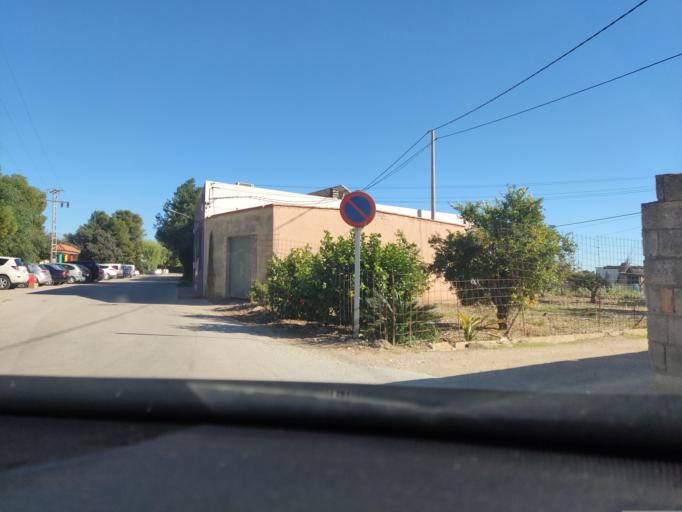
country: ES
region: Valencia
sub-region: Provincia de Alicante
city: els Poblets
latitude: 38.8496
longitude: 0.0197
